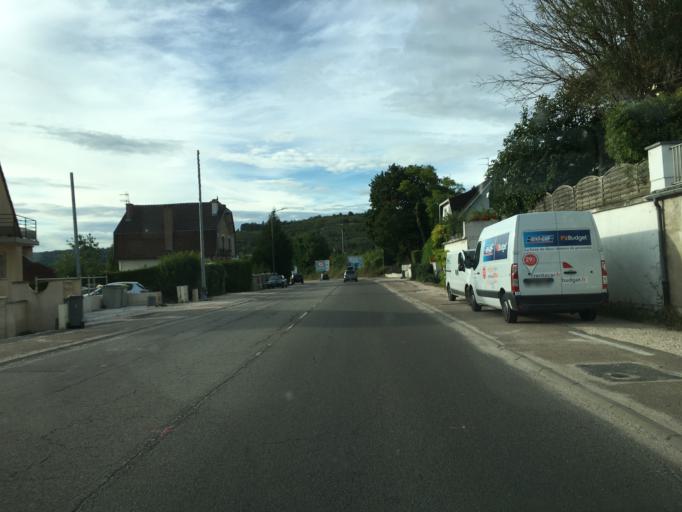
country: FR
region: Bourgogne
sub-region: Departement de la Cote-d'Or
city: Talant
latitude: 47.3329
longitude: 4.9888
